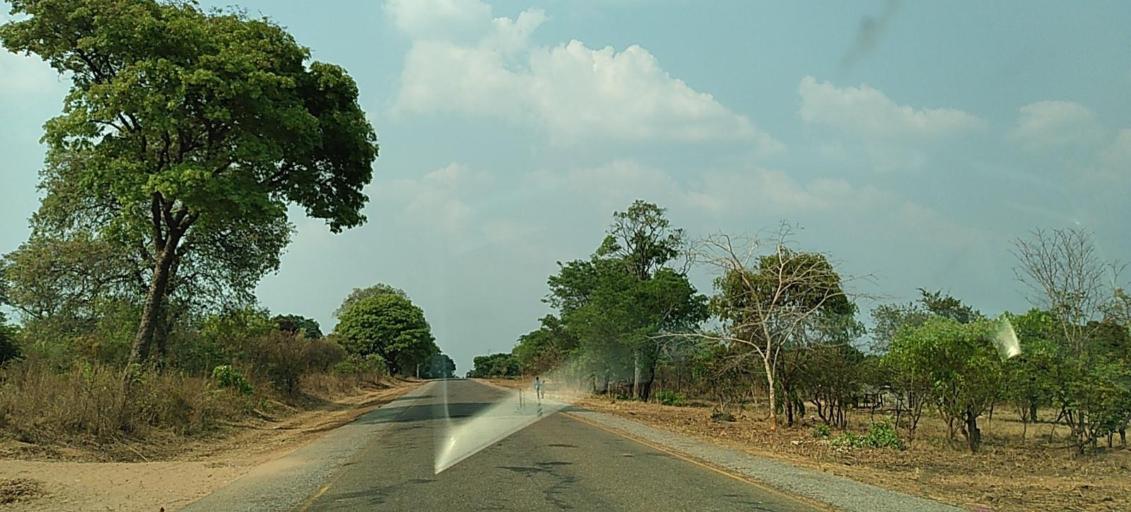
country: ZM
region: North-Western
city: Kabompo
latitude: -13.6265
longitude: 24.1126
